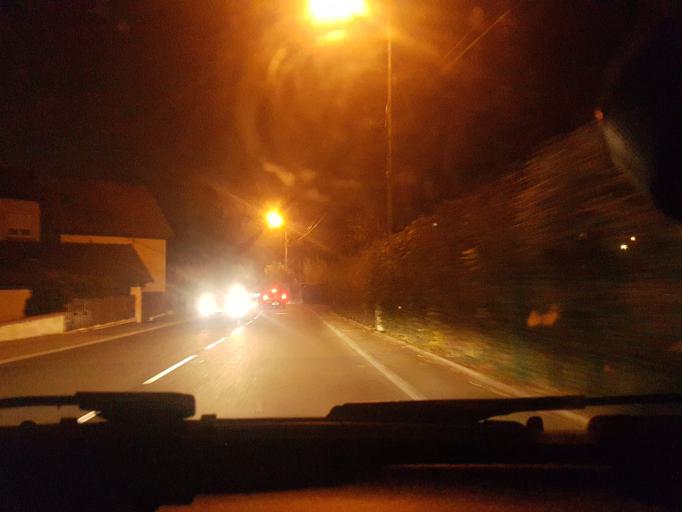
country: FR
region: Franche-Comte
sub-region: Territoire de Belfort
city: Danjoutin
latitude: 47.6154
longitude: 6.8709
